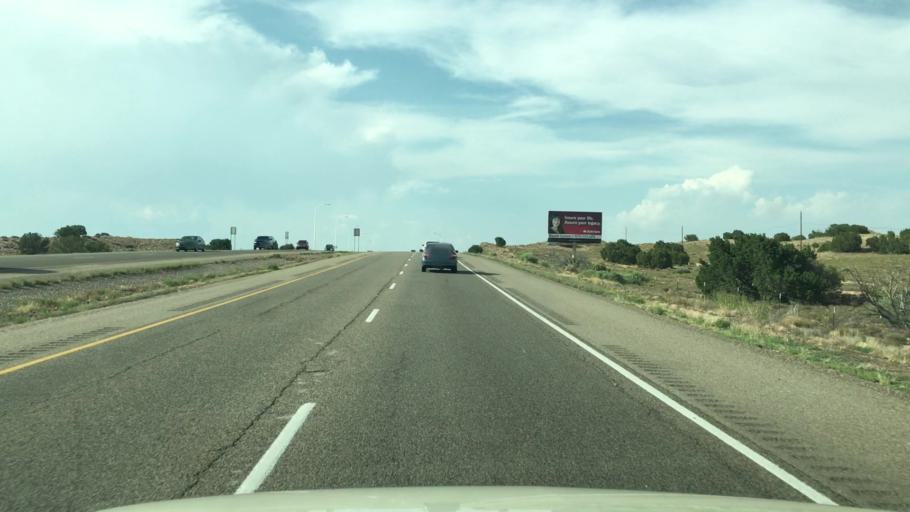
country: US
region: New Mexico
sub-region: Santa Fe County
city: Pojoaque
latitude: 35.9203
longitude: -106.0167
